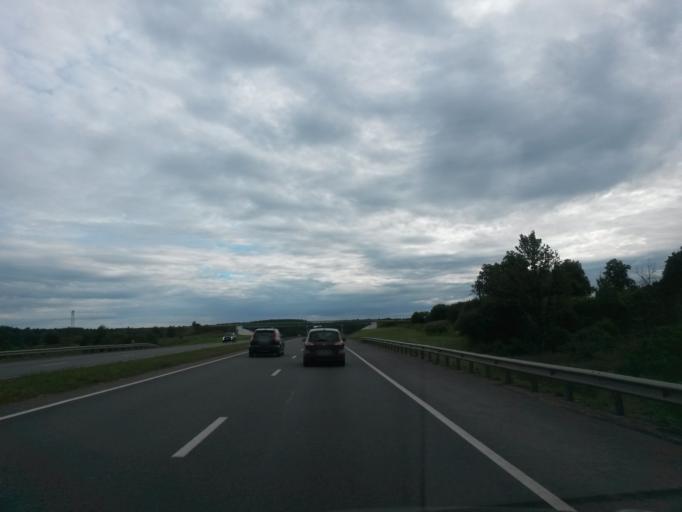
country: RU
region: Jaroslavl
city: Semibratovo
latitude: 57.3859
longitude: 39.6225
